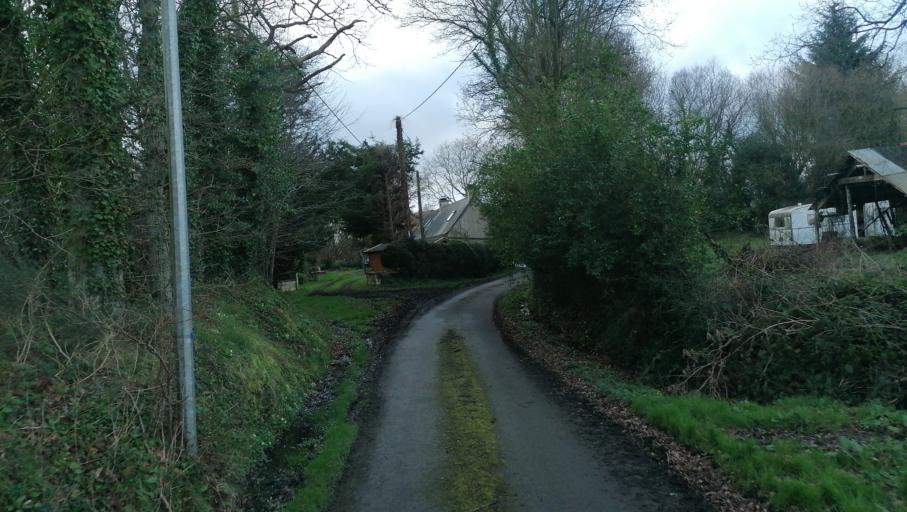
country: FR
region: Brittany
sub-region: Departement des Cotes-d'Armor
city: Pommerit-le-Vicomte
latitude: 48.6446
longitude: -3.0782
